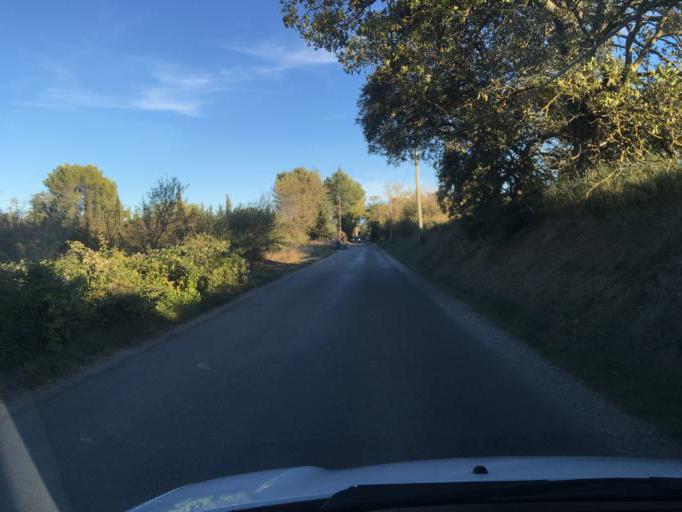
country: FR
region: Provence-Alpes-Cote d'Azur
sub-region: Departement du Vaucluse
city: Carpentras
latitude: 44.0590
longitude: 5.0766
